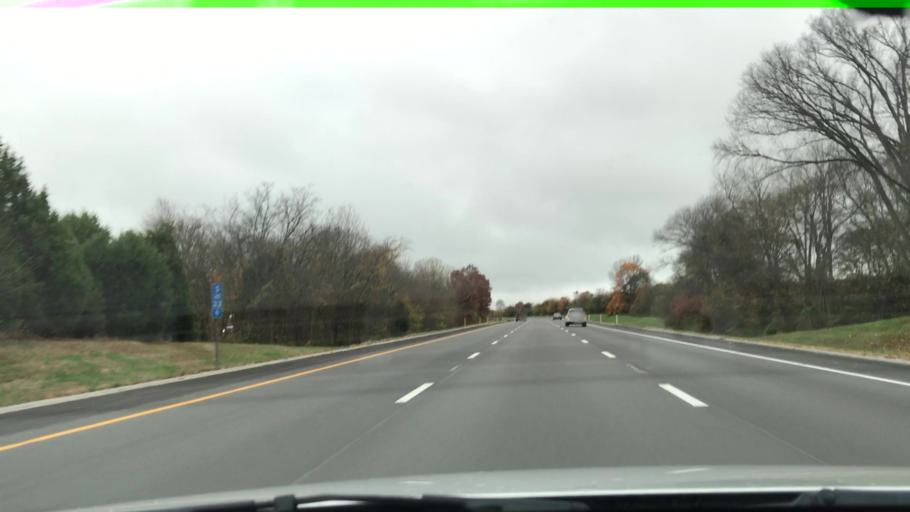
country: US
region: Kentucky
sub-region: Edmonson County
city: Brownsville
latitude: 37.0181
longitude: -86.2698
